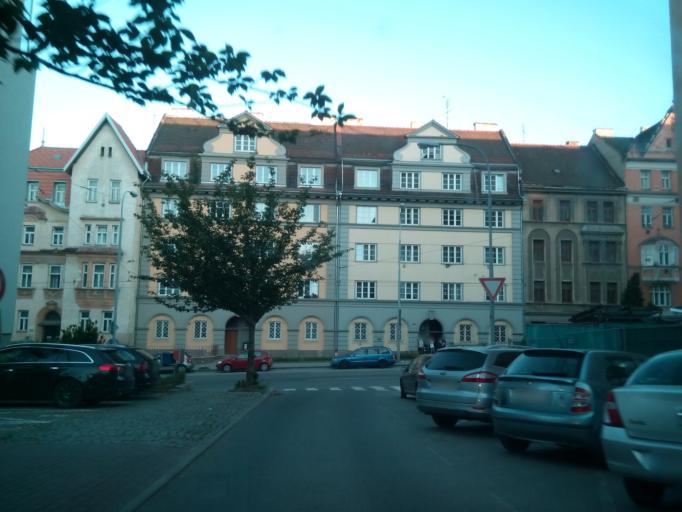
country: CZ
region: South Moravian
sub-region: Mesto Brno
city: Brno
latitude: 49.2044
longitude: 16.6221
